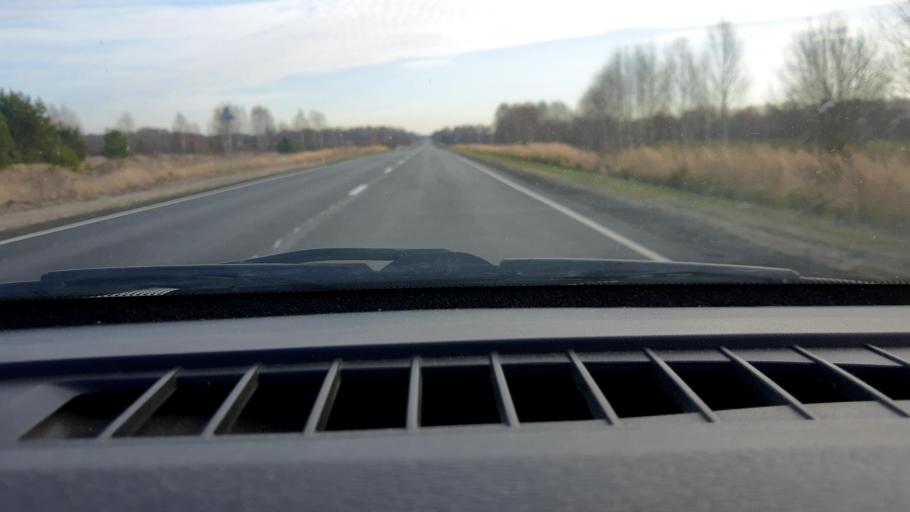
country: RU
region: Nizjnij Novgorod
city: Novaya Balakhna
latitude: 56.5866
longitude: 43.6723
